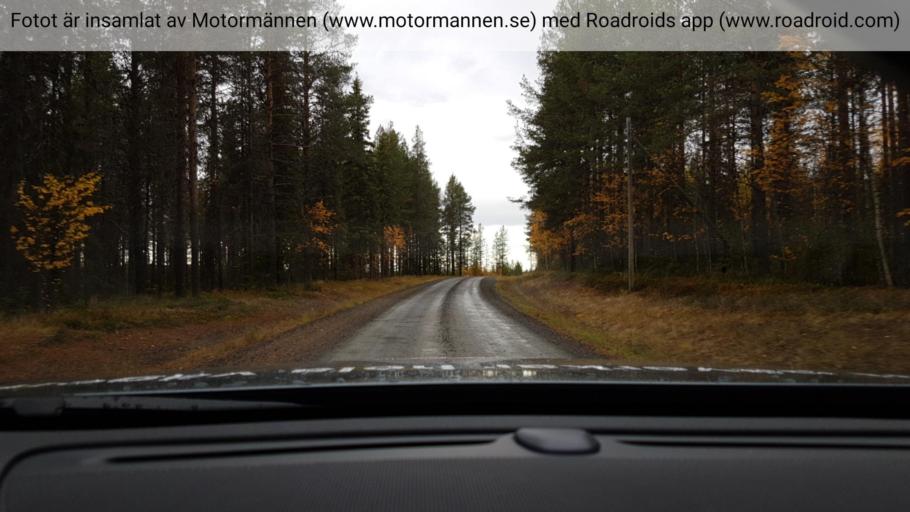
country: SE
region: Norrbotten
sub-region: Pajala Kommun
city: Pajala
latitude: 67.1281
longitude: 22.6625
